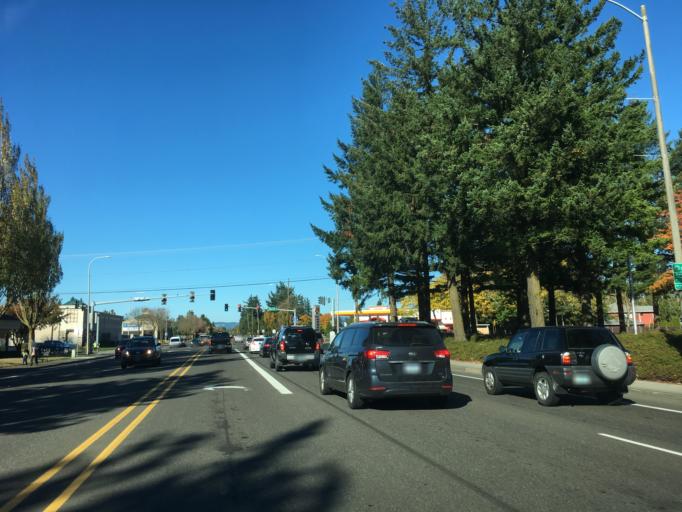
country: US
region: Oregon
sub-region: Multnomah County
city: Troutdale
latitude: 45.5181
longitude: -122.3984
